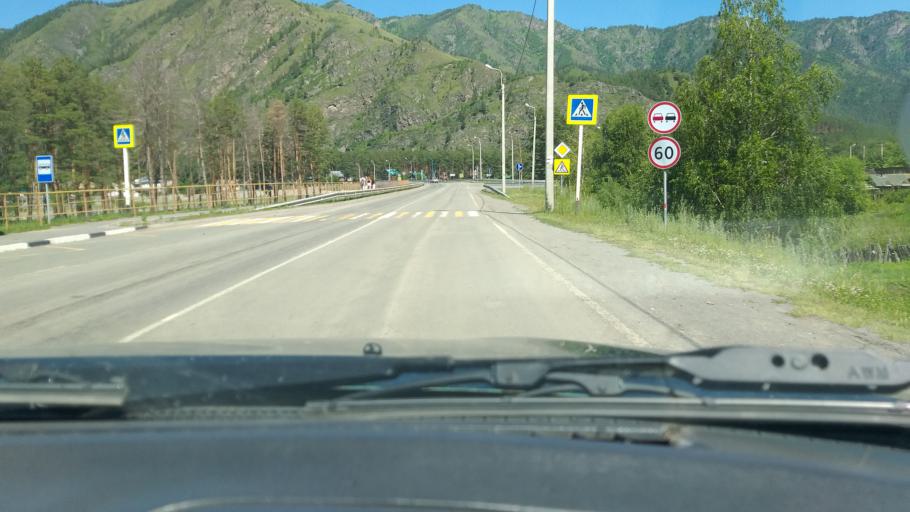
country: RU
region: Altay
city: Chemal
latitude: 51.3904
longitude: 86.0180
